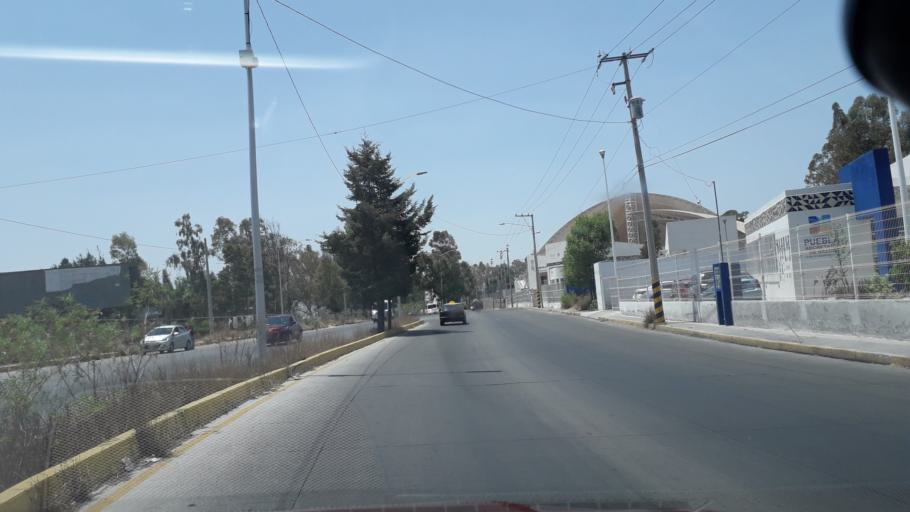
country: MX
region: Puebla
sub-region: Puebla
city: Galaxia la Calera
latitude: 19.0054
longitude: -98.1838
